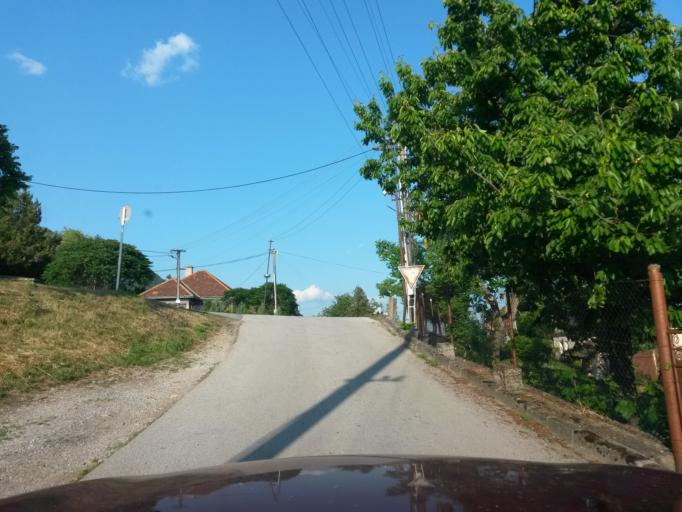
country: SK
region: Kosicky
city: Roznava
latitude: 48.5958
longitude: 20.6751
